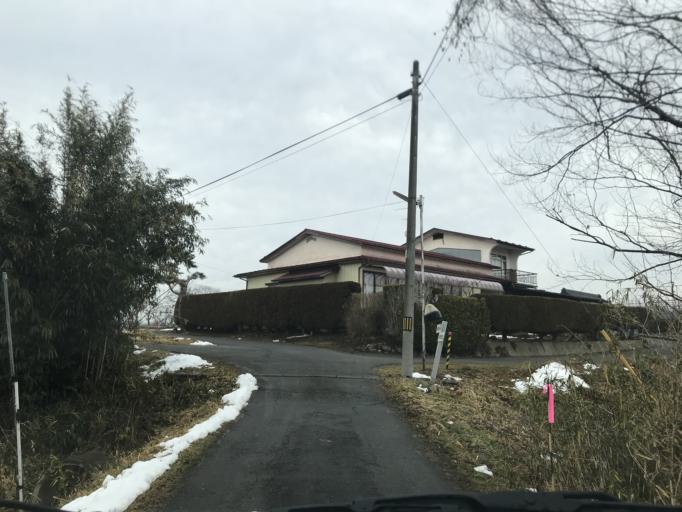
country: JP
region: Iwate
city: Mizusawa
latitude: 39.1809
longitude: 141.1396
